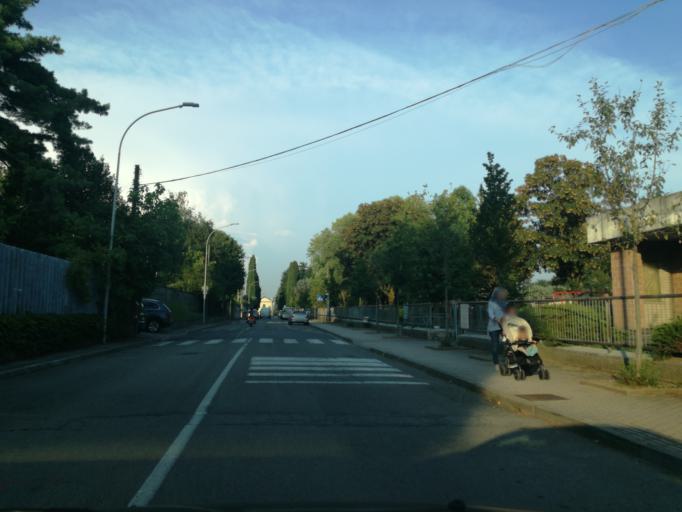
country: IT
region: Lombardy
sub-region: Provincia di Lecco
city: Paderno d'Adda
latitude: 45.6816
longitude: 9.4471
